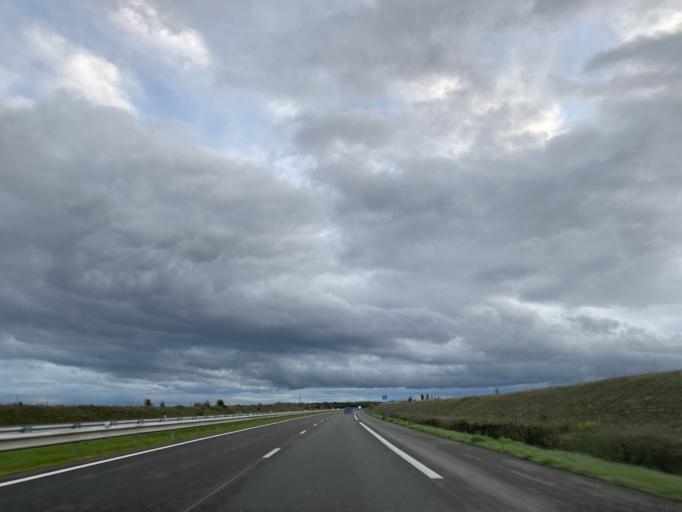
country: FR
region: Centre
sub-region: Departement du Cher
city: Plaimpied-Givaudins
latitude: 46.9963
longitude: 2.4066
